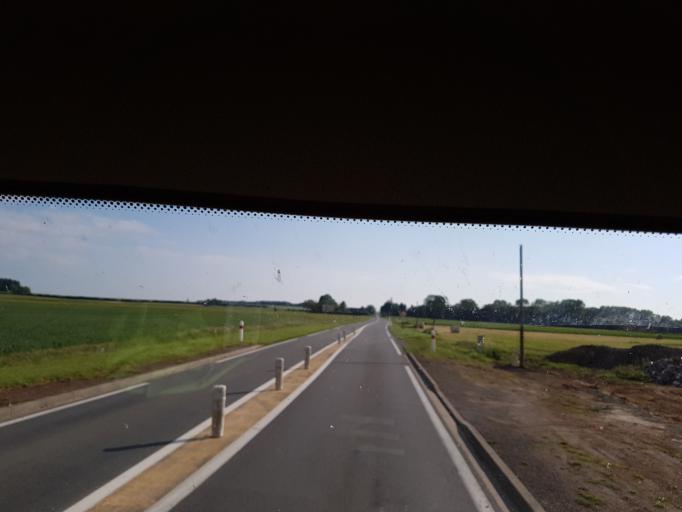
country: FR
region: Picardie
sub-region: Departement de la Somme
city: Crecy-en-Ponthieu
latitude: 50.2306
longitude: 1.9360
